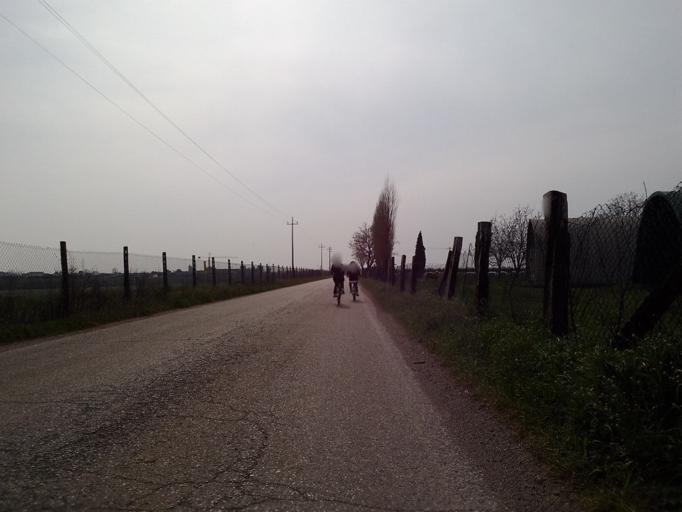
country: IT
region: Veneto
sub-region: Provincia di Verona
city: Alpo
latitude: 45.3795
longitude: 10.9055
